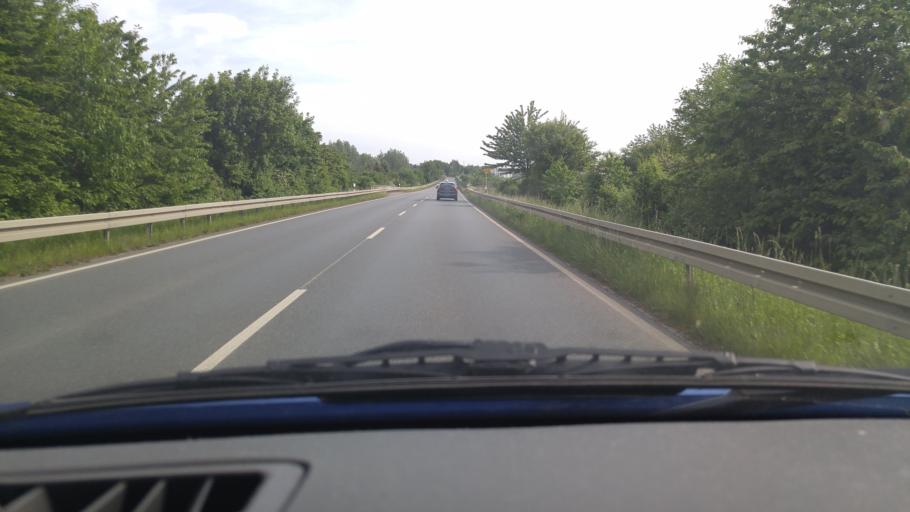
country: DE
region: Hesse
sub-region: Regierungsbezirk Darmstadt
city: Wolfersheim
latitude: 50.3903
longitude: 8.8124
